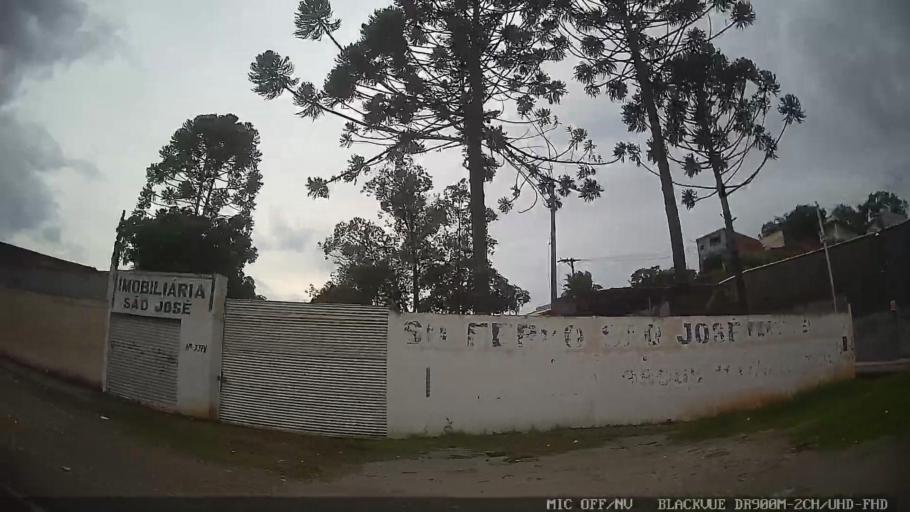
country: BR
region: Sao Paulo
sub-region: Itaquaquecetuba
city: Itaquaquecetuba
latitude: -23.4733
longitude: -46.2972
